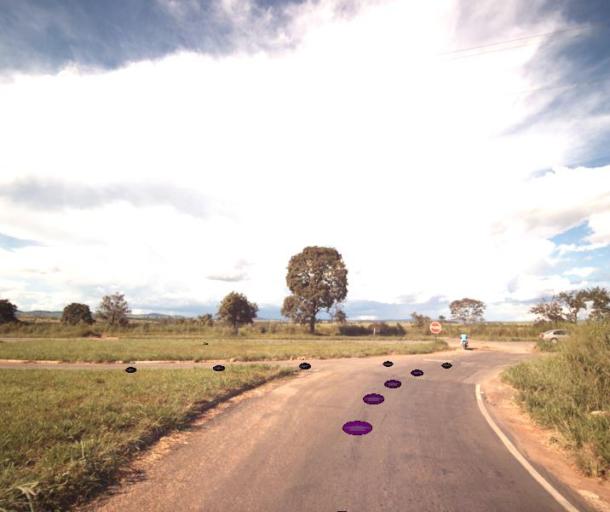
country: BR
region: Goias
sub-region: Rialma
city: Rialma
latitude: -15.4744
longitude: -49.4964
